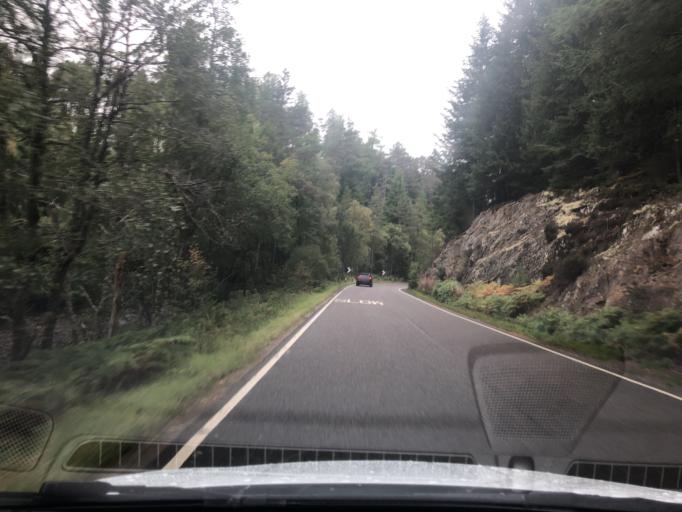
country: GB
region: Scotland
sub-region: Highland
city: Kingussie
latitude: 56.9815
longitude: -4.3624
